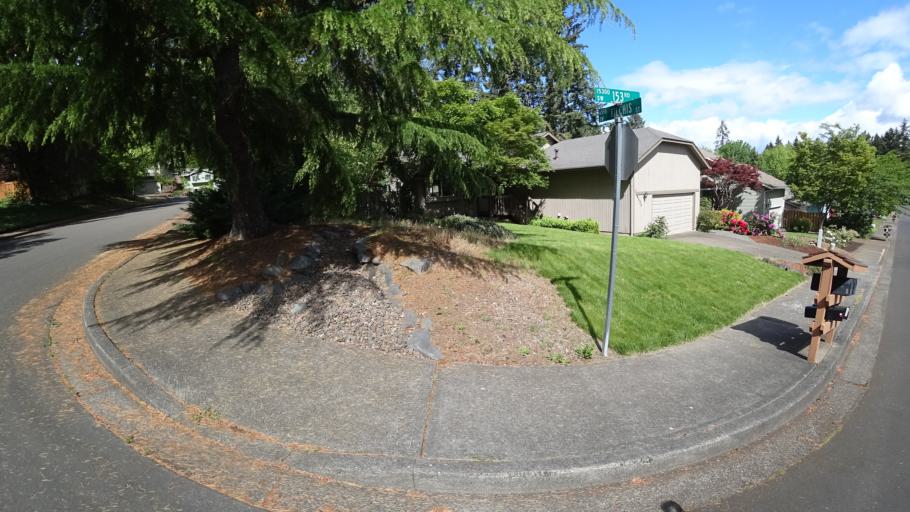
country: US
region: Oregon
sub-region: Washington County
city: Beaverton
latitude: 45.4725
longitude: -122.8354
